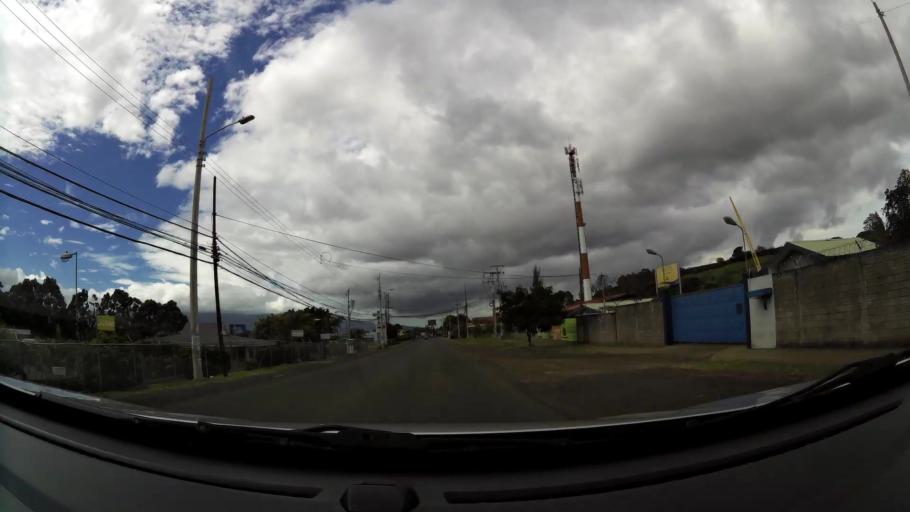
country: CR
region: Cartago
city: Tres Rios
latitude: 9.9096
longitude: -83.9970
